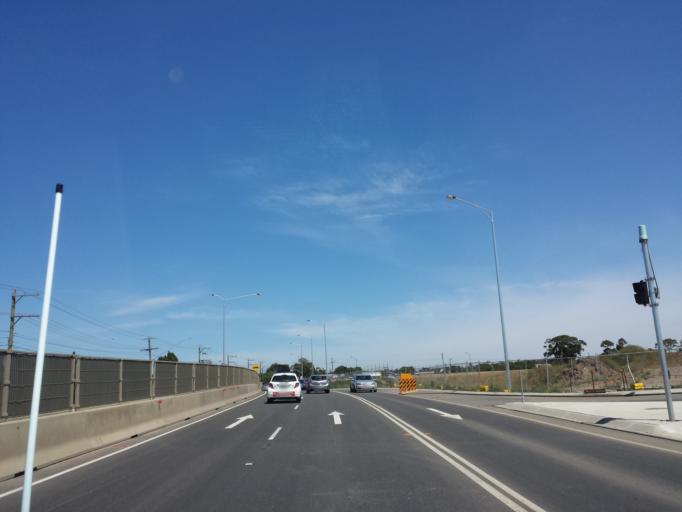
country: AU
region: Victoria
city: Heatherton
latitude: -37.9562
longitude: 145.1034
